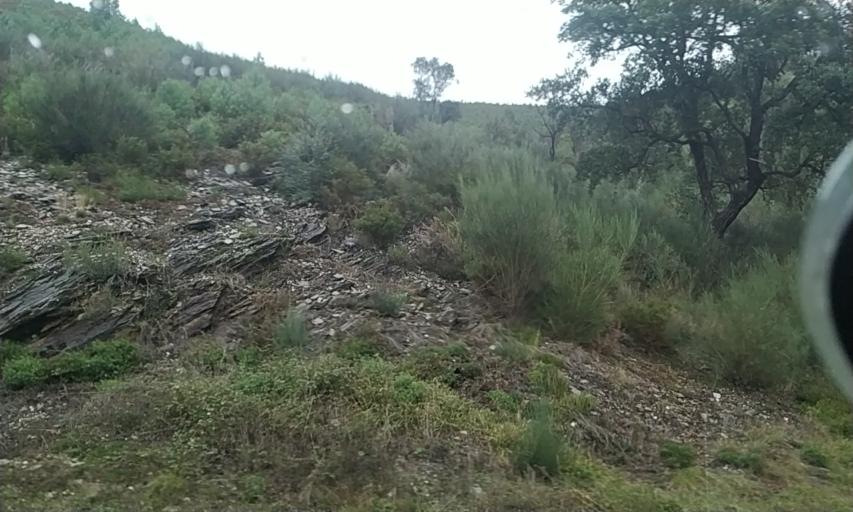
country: PT
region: Vila Real
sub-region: Mondim de Basto
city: Mondim de Basto
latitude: 41.3545
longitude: -7.9085
